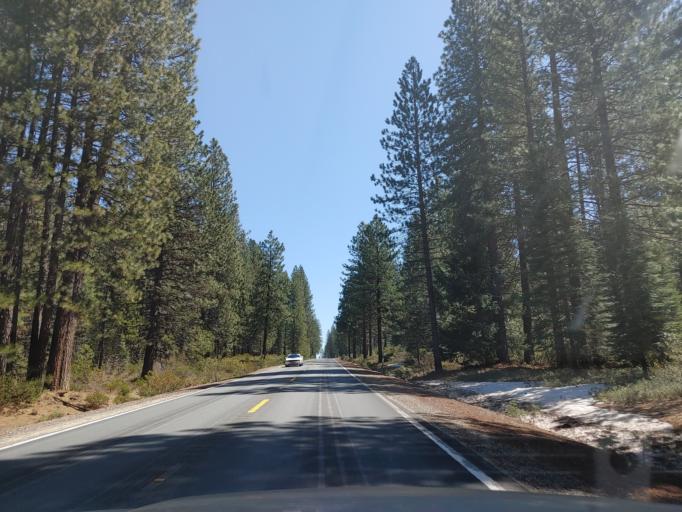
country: US
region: California
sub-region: Siskiyou County
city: McCloud
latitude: 41.2668
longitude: -121.8923
